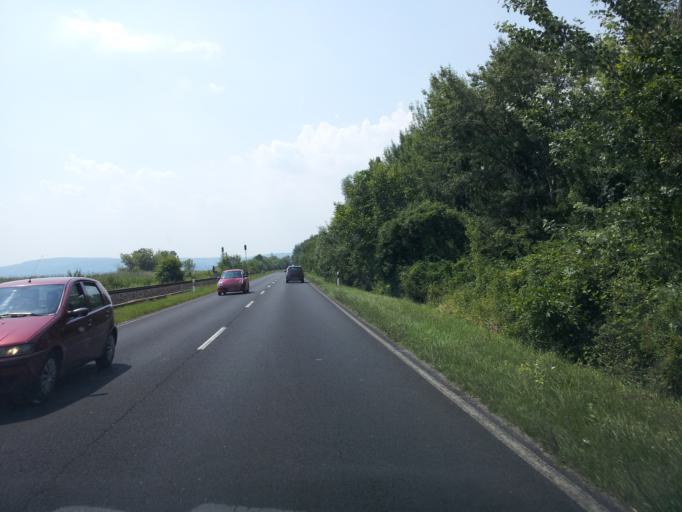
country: HU
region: Veszprem
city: Balatonkenese
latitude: 47.0387
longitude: 18.0802
